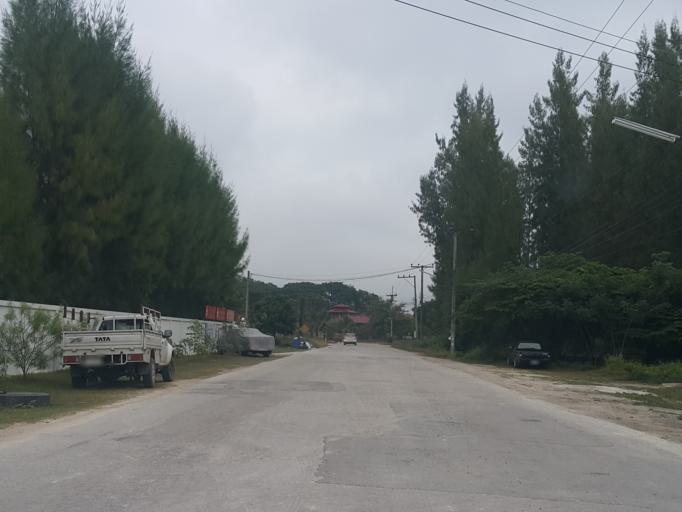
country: TH
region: Lampang
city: Lampang
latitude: 18.3232
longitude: 99.4890
